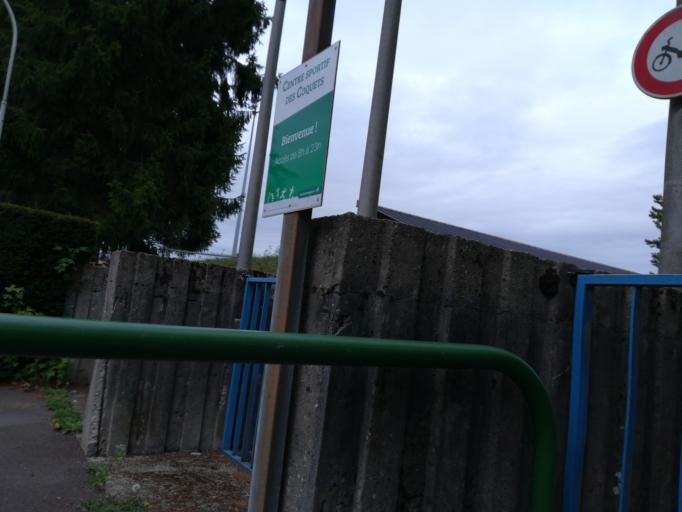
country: FR
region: Haute-Normandie
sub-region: Departement de la Seine-Maritime
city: Mont-Saint-Aignan
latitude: 49.4658
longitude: 1.0751
